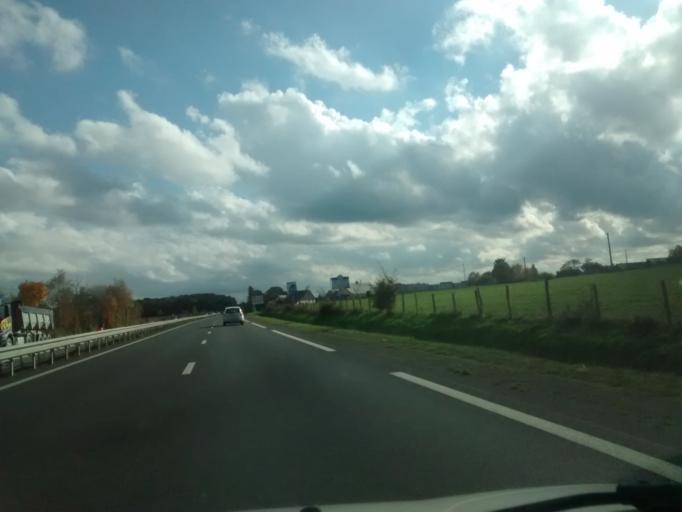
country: FR
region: Brittany
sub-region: Departement d'Ille-et-Vilaine
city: Chantepie
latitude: 48.0711
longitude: -1.6246
